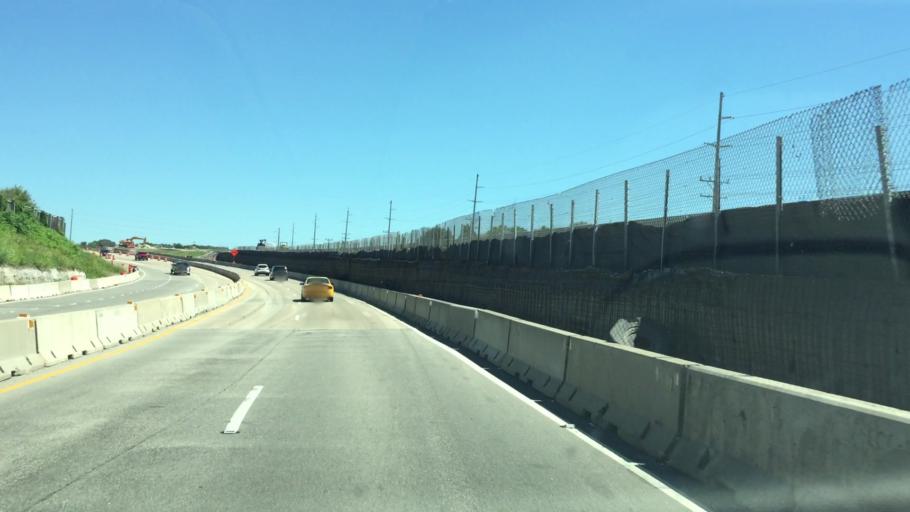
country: US
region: Wisconsin
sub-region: Winnebago County
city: Menasha
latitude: 44.2269
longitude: -88.4424
